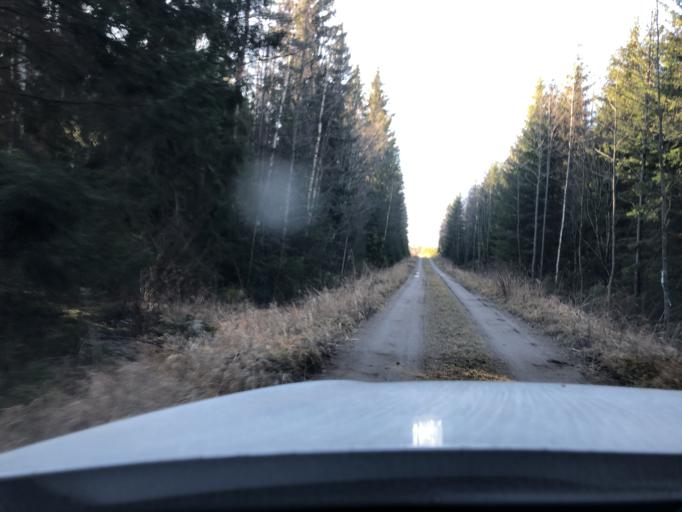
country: SE
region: Gaevleborg
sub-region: Gavle Kommun
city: Hedesunda
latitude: 60.3053
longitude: 16.8971
